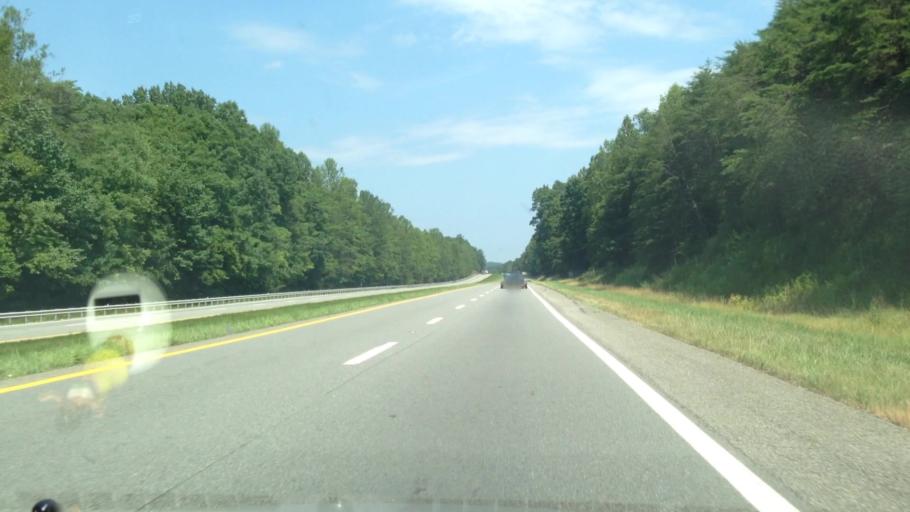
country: US
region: Virginia
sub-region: Henry County
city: Horse Pasture
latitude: 36.6678
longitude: -79.9285
